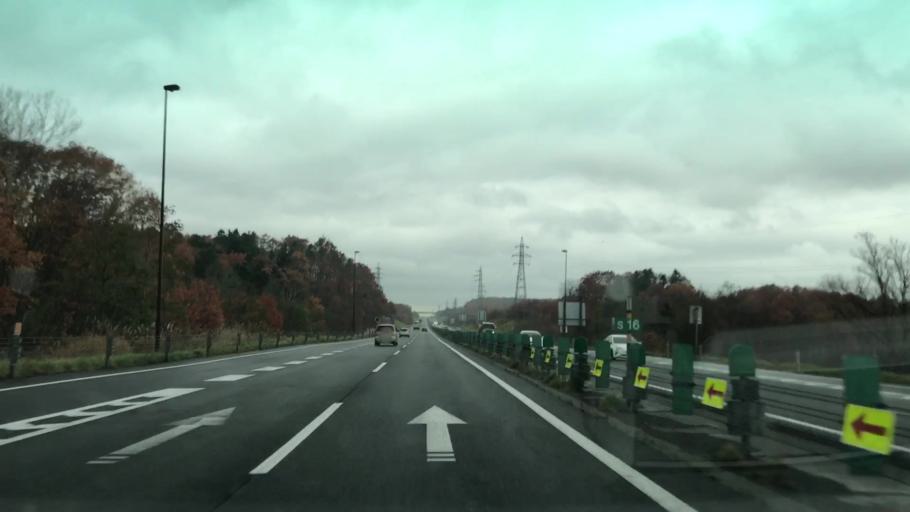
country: JP
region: Hokkaido
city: Kitahiroshima
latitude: 42.9535
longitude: 141.5095
